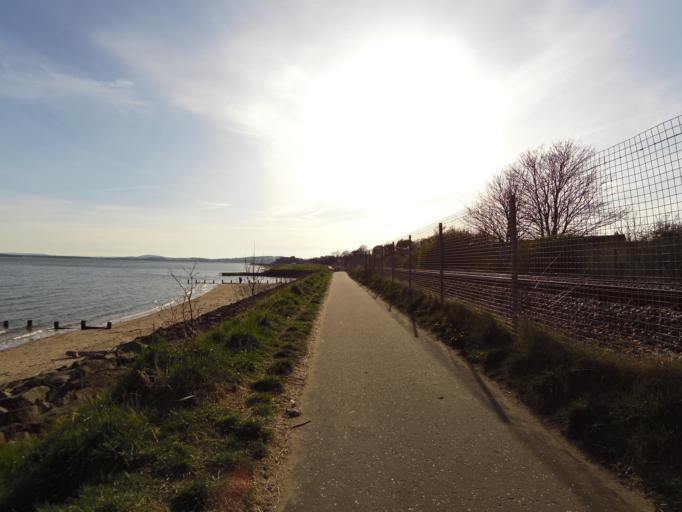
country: GB
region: Scotland
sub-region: Fife
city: Tayport
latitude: 56.4758
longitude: -2.8354
